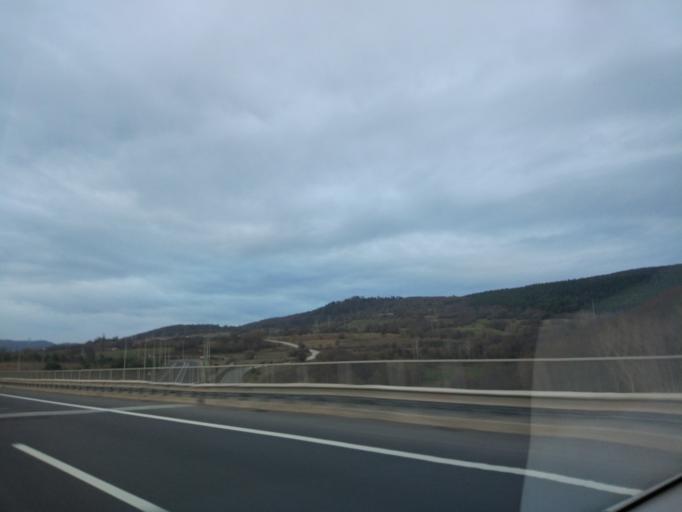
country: TR
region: Bolu
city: Bolu
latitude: 40.7215
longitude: 31.4800
